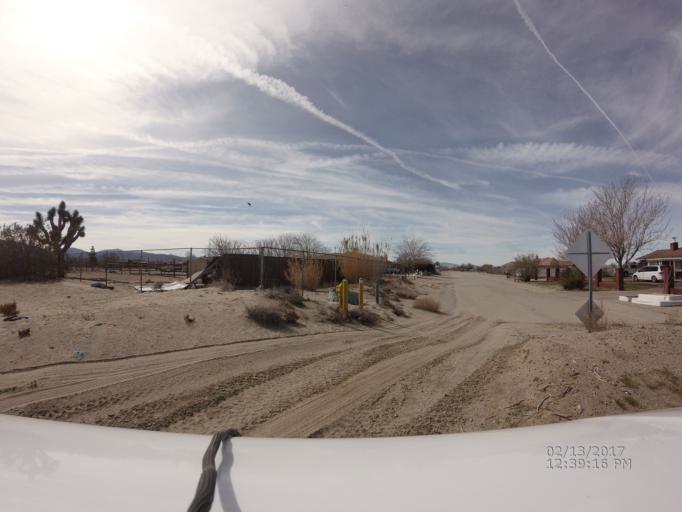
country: US
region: California
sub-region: Los Angeles County
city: Littlerock
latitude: 34.5707
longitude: -117.9185
